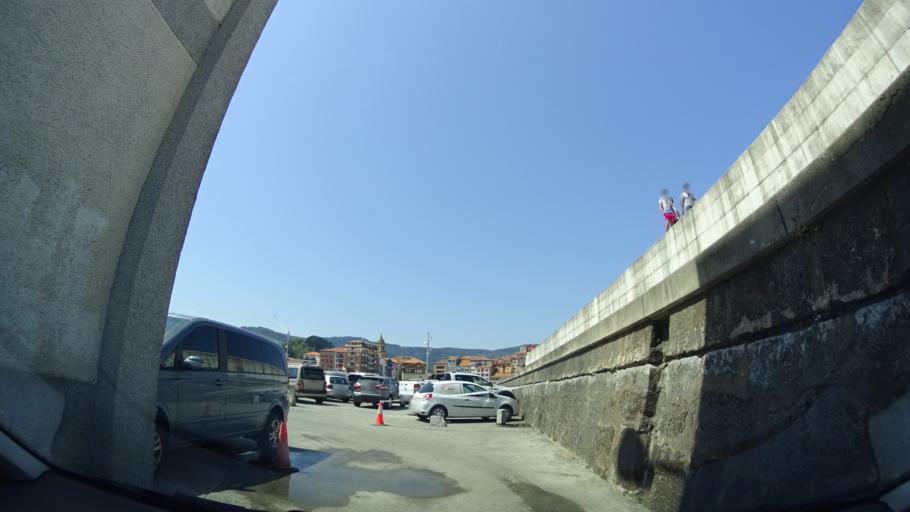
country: ES
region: Basque Country
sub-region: Bizkaia
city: Bermeo
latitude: 43.4206
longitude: -2.7179
